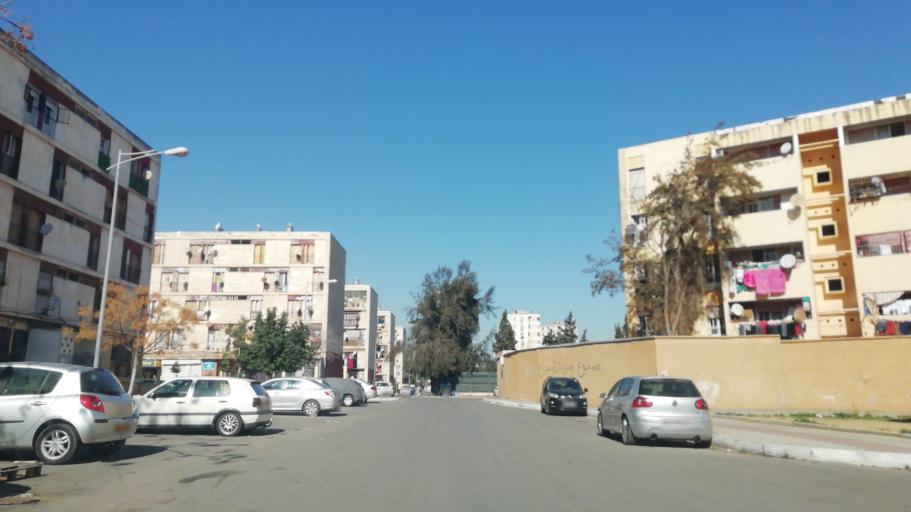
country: DZ
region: Oran
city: Oran
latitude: 35.6787
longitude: -0.6384
